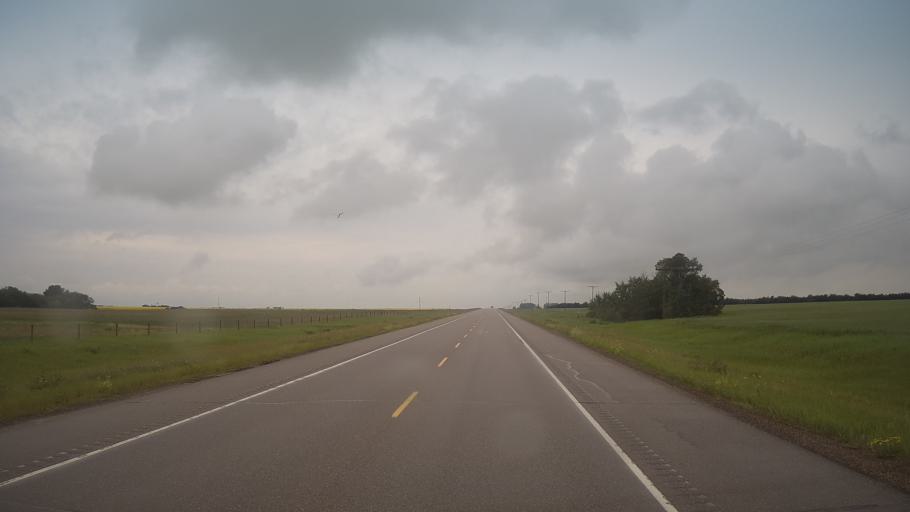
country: CA
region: Saskatchewan
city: Unity
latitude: 52.4349
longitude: -108.9468
